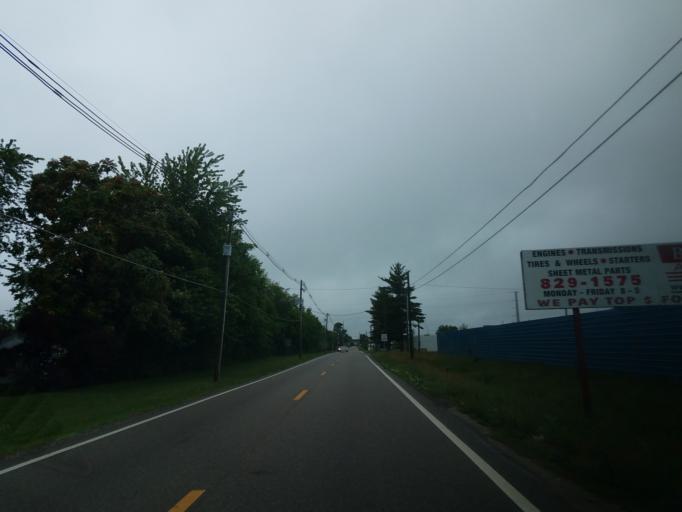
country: US
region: Illinois
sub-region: McLean County
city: Bloomington
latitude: 40.4540
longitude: -88.9814
